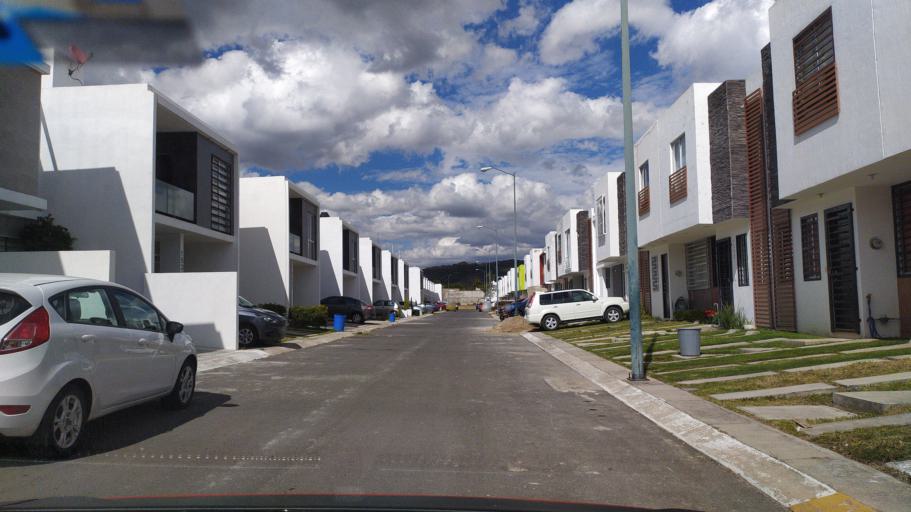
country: MX
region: Jalisco
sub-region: Tlajomulco de Zuniga
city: Palomar
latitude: 20.6314
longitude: -103.4814
